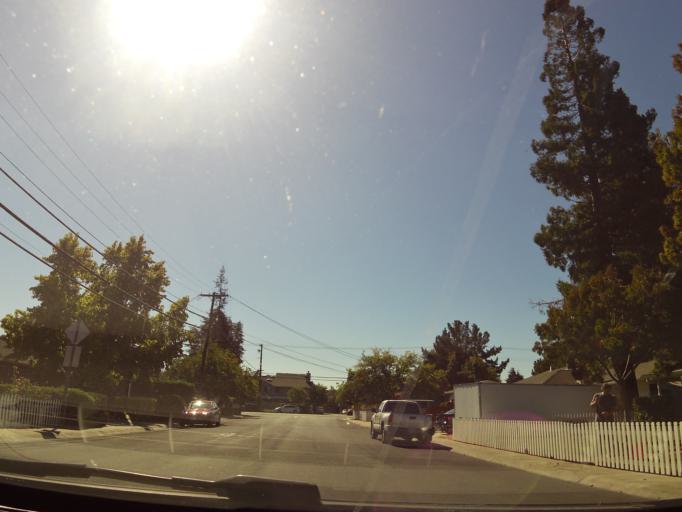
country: US
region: California
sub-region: Santa Clara County
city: Campbell
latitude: 37.2878
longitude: -121.9574
